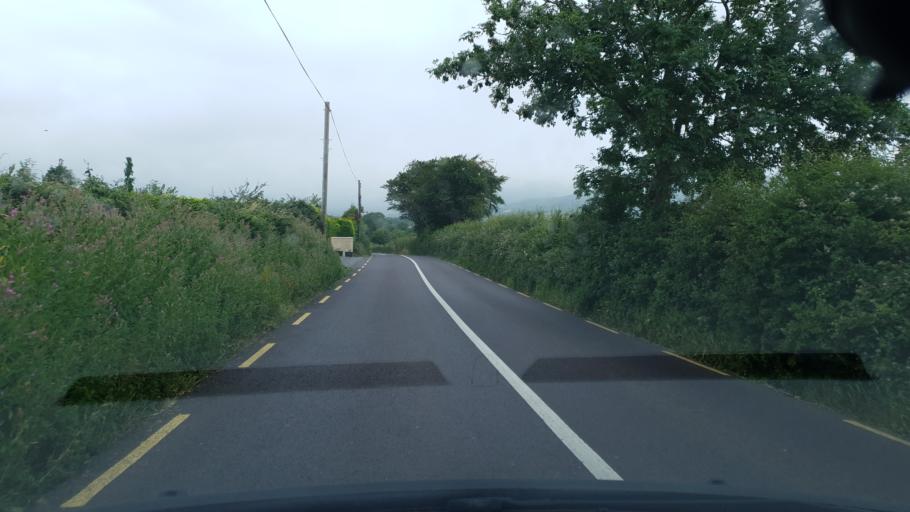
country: IE
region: Munster
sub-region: Ciarrai
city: Tralee
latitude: 52.1626
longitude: -9.6936
